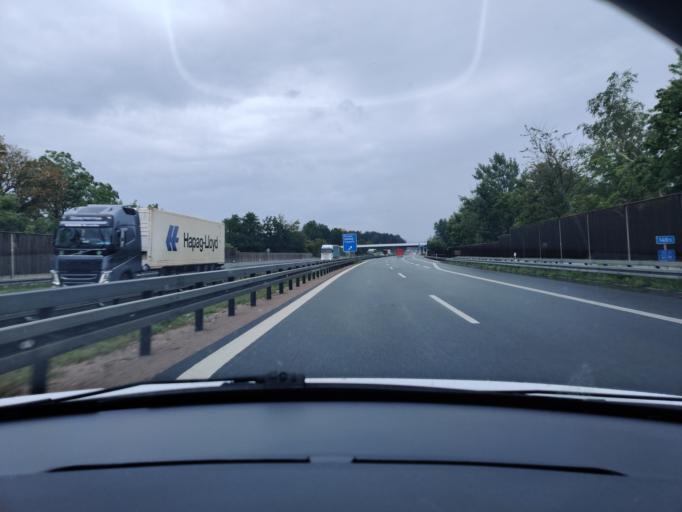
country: DE
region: Bavaria
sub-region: Upper Palatinate
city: Pfreimd
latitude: 49.4936
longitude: 12.1888
